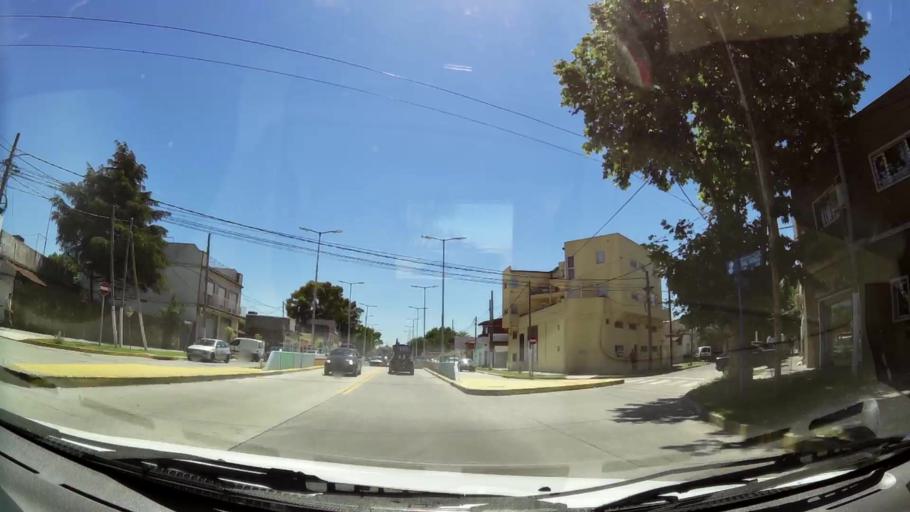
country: AR
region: Buenos Aires
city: Caseros
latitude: -34.5922
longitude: -58.5661
